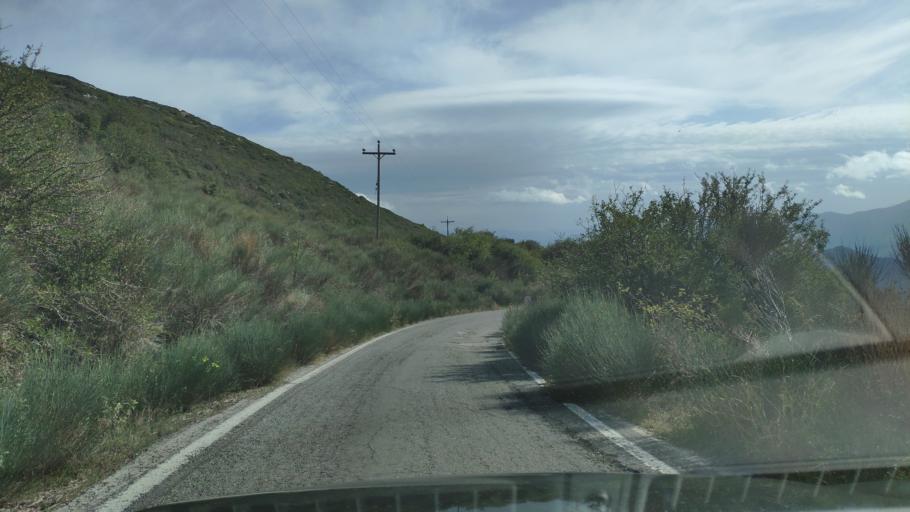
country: GR
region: Peloponnese
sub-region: Nomos Arkadias
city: Dimitsana
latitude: 37.5743
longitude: 22.0189
